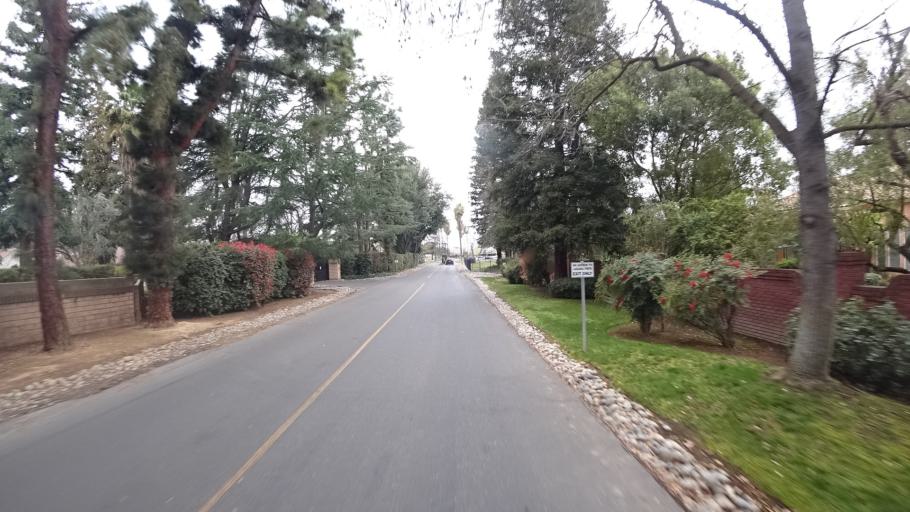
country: US
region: California
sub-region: Fresno County
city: Fresno
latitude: 36.8483
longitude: -119.8499
